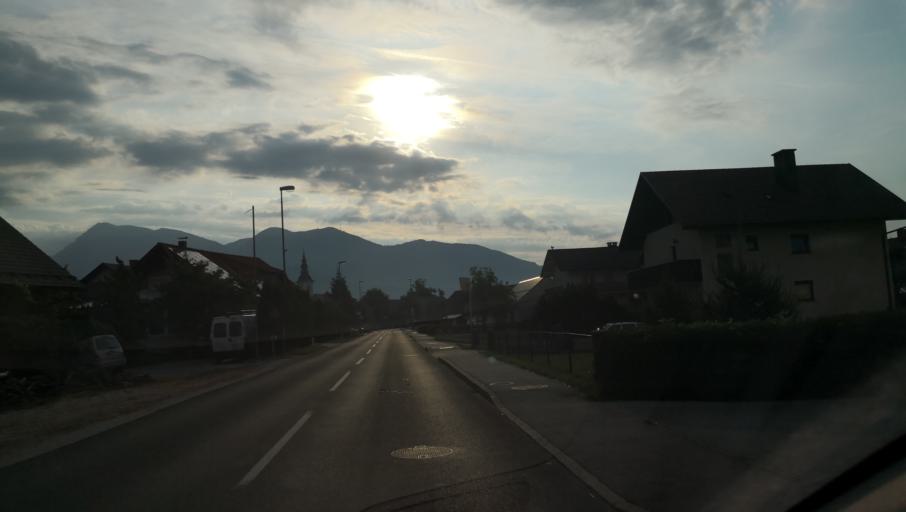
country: SI
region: Kranj
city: Britof
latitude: 46.2695
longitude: 14.4128
